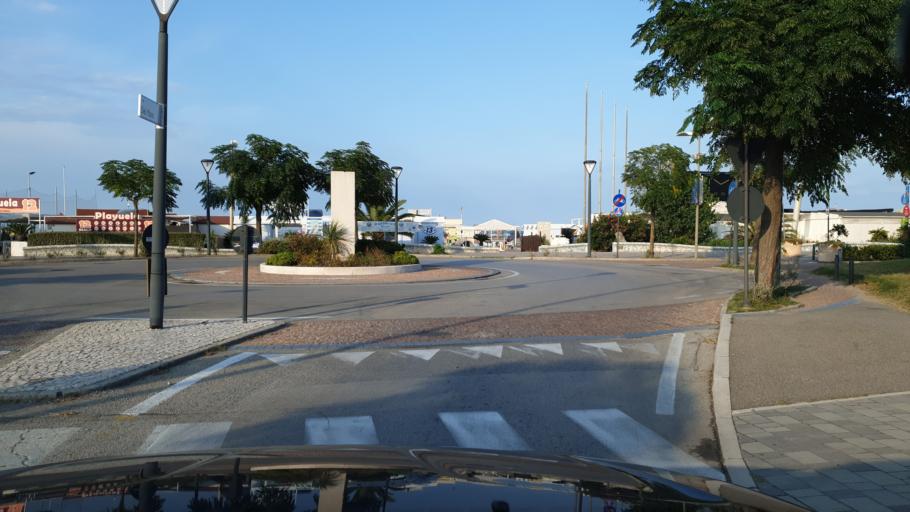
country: IT
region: Emilia-Romagna
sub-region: Provincia di Rimini
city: Misano Adriatico
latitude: 43.9838
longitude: 12.6915
